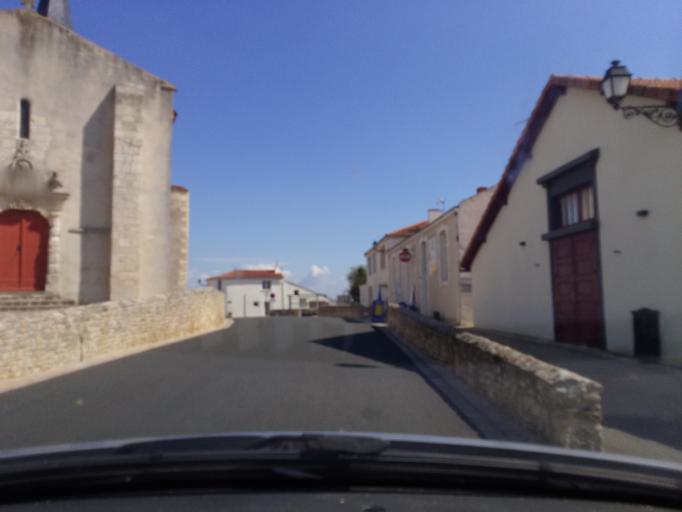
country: FR
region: Pays de la Loire
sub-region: Departement de la Vendee
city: Triaize
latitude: 46.4067
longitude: -1.2678
